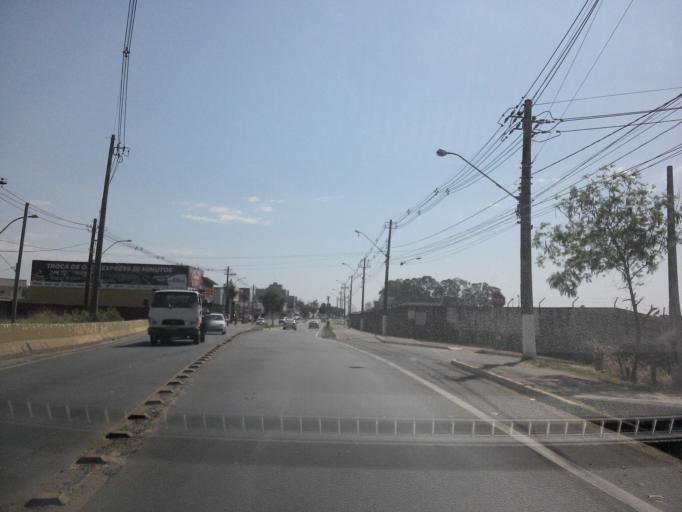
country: BR
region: Sao Paulo
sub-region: Hortolandia
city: Hortolandia
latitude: -22.8846
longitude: -47.2308
